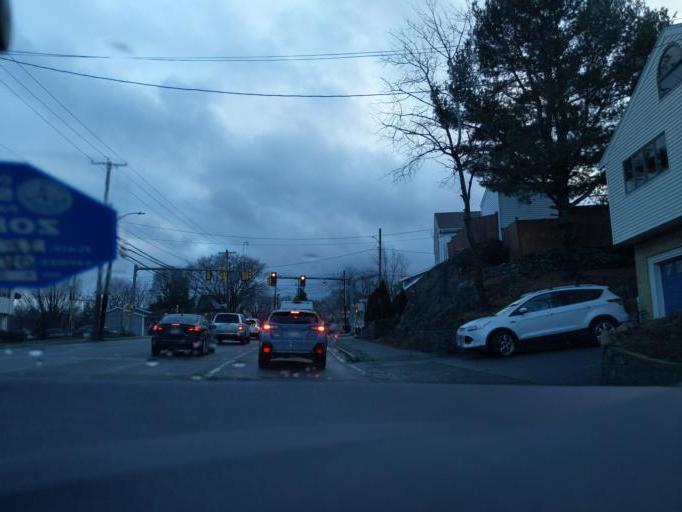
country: US
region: Massachusetts
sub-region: Essex County
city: Salem
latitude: 42.5095
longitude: -70.9108
